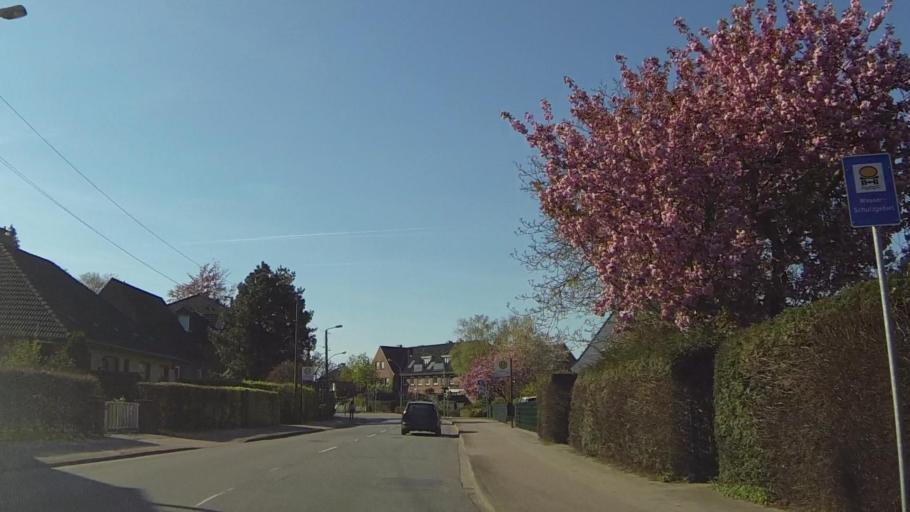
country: DE
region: Schleswig-Holstein
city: Pinneberg
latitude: 53.6475
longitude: 9.7887
